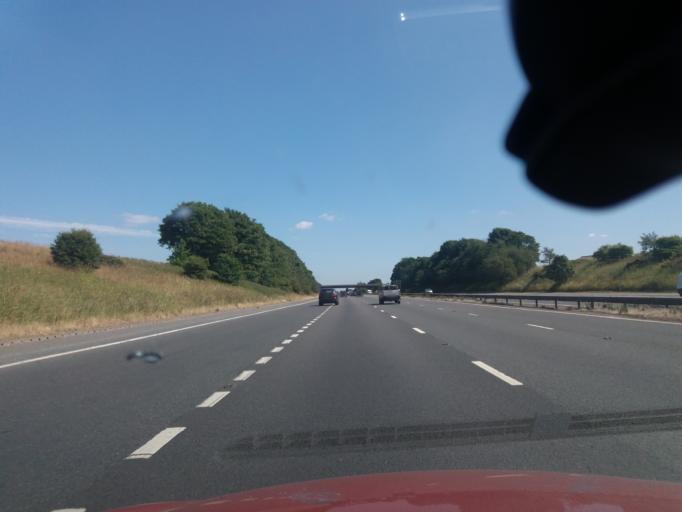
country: GB
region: England
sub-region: Borough of Bolton
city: Westhoughton
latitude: 53.5718
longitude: -2.5403
